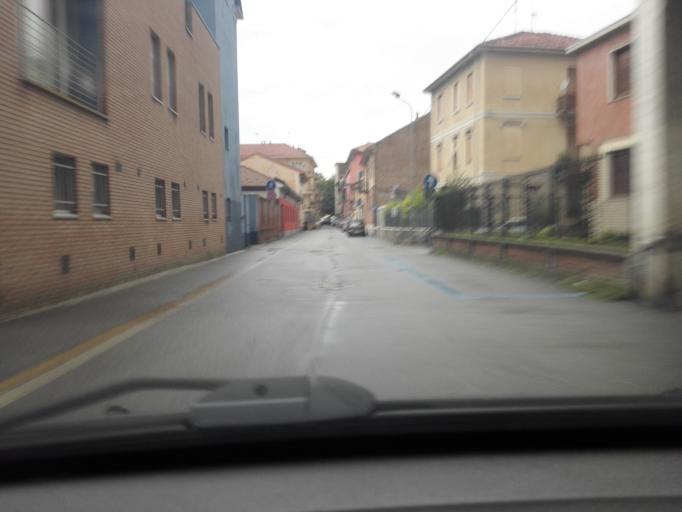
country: IT
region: Piedmont
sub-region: Provincia di Alessandria
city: Alessandria
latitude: 44.9184
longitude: 8.6162
